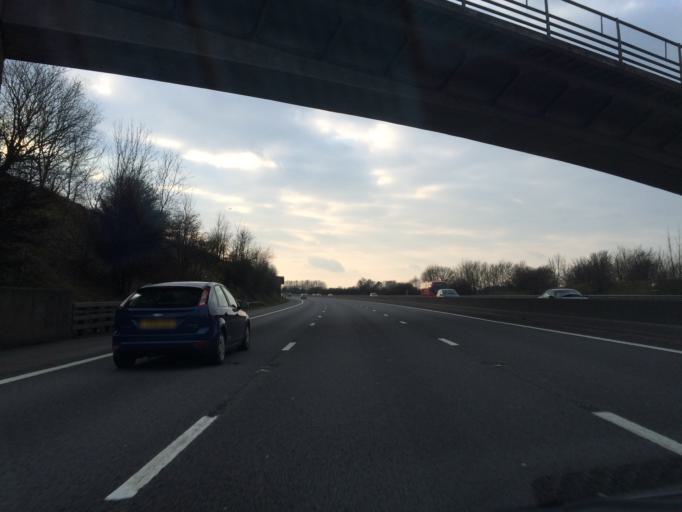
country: GB
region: England
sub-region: Wiltshire
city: Aldbourne
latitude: 51.5054
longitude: -1.5959
